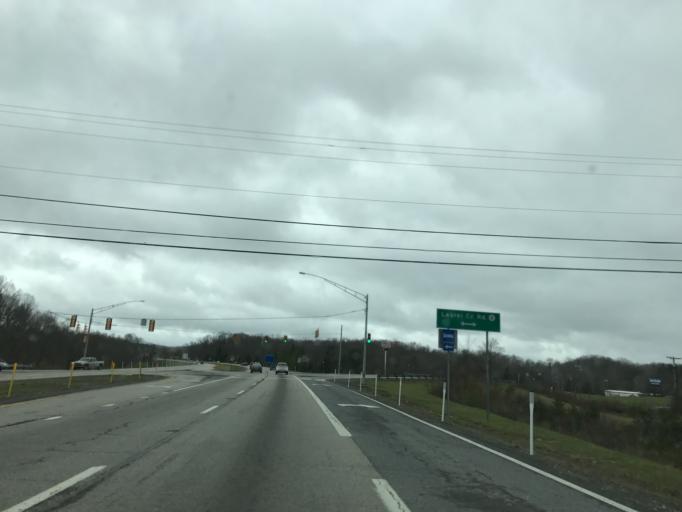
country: US
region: West Virginia
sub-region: Fayette County
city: Fayetteville
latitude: 38.0506
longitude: -81.1181
